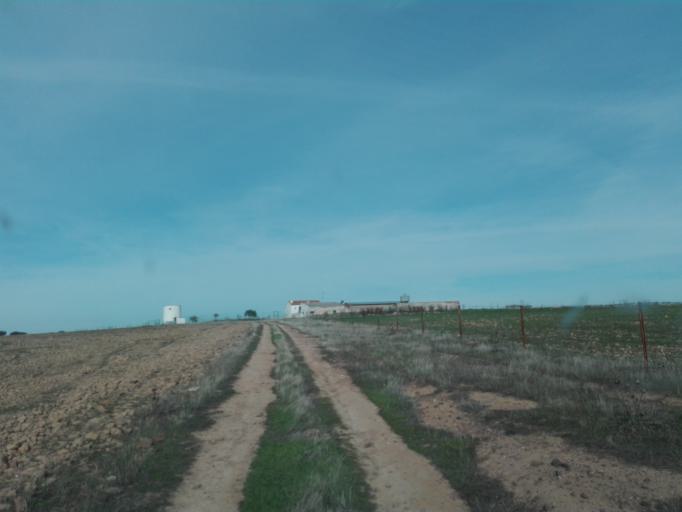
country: ES
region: Extremadura
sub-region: Provincia de Badajoz
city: Campillo de Llerena
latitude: 38.4722
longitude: -5.8902
